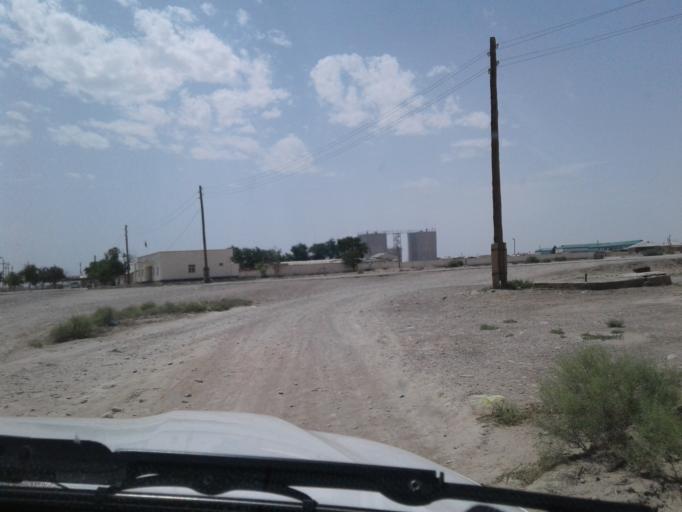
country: IR
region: Razavi Khorasan
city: Kalat-e Naderi
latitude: 37.2002
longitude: 60.0249
